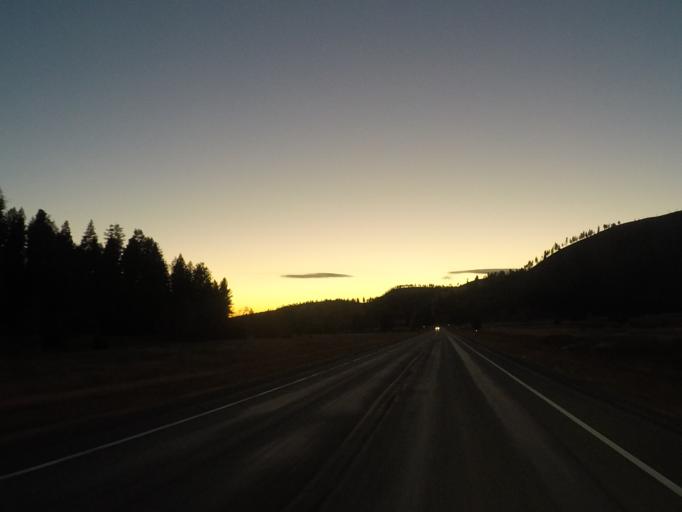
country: US
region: Montana
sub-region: Missoula County
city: Seeley Lake
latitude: 47.0305
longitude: -113.2670
